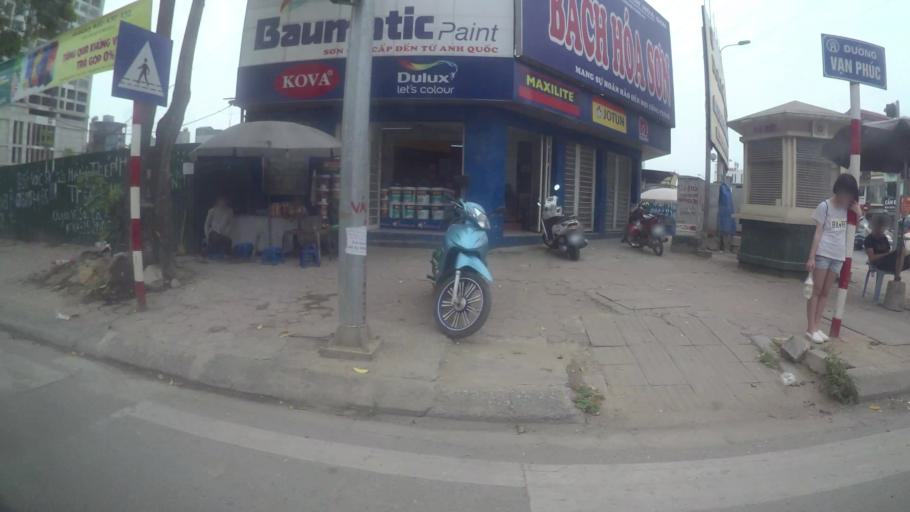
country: VN
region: Ha Noi
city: Ha Dong
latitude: 20.9823
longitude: 105.7704
